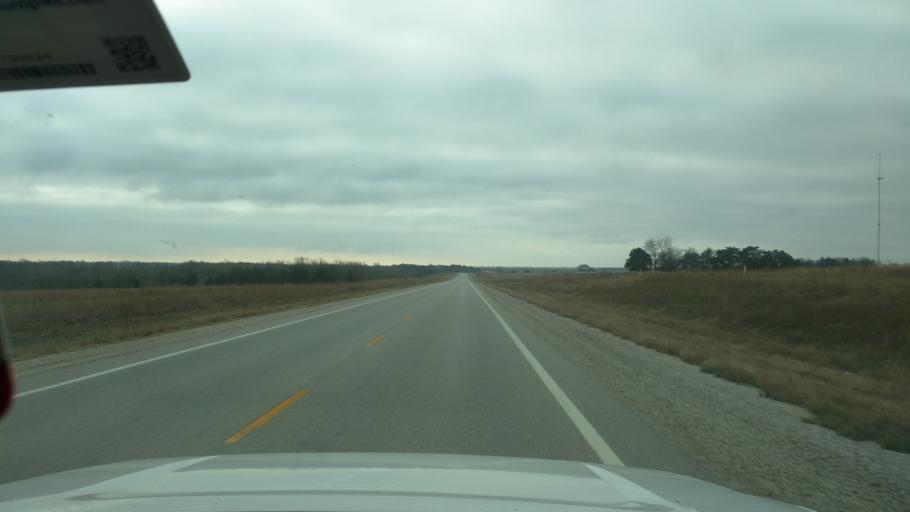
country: US
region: Kansas
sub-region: Elk County
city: Howard
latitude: 37.5540
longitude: -96.2533
